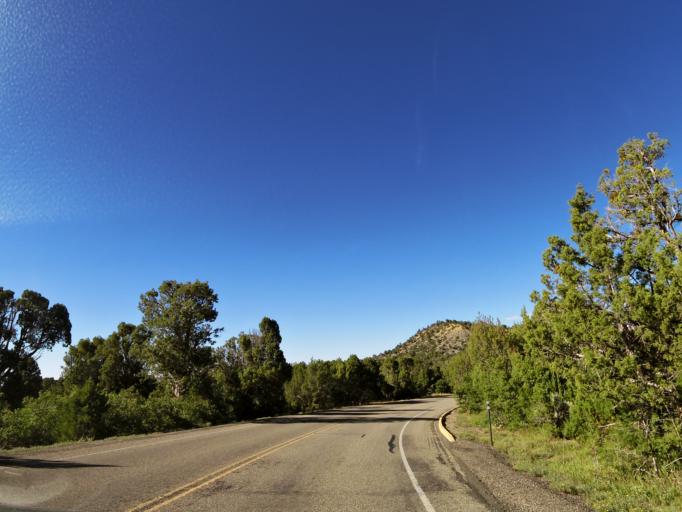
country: US
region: Colorado
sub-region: Montezuma County
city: Mancos
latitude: 37.3284
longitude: -108.4183
